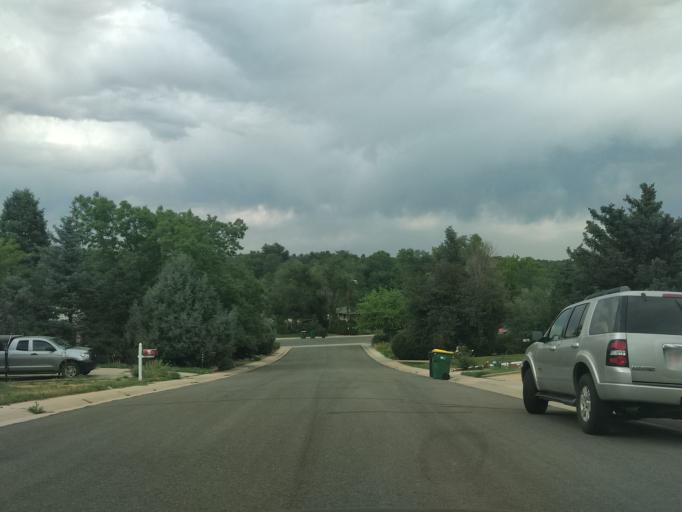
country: US
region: Colorado
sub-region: Jefferson County
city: Lakewood
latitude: 39.6979
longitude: -105.0932
